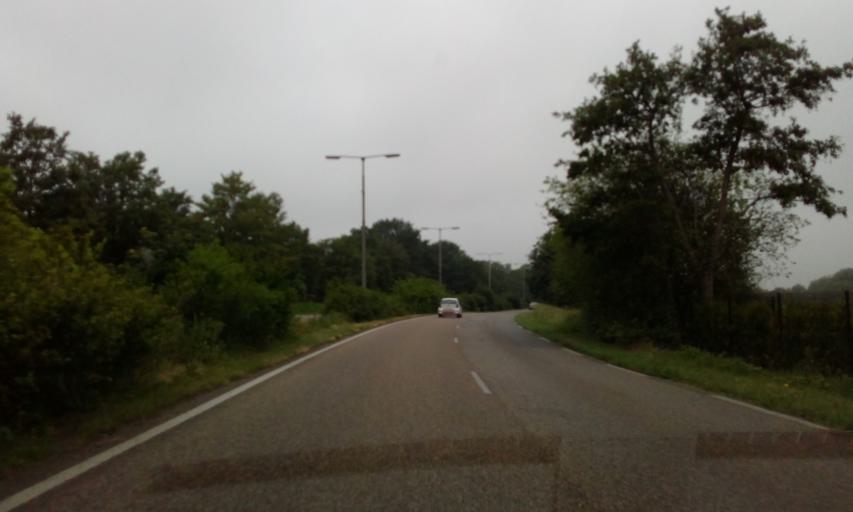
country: NL
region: South Holland
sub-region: Gemeente Ridderkerk
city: Ridderkerk
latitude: 51.8751
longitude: 4.6016
